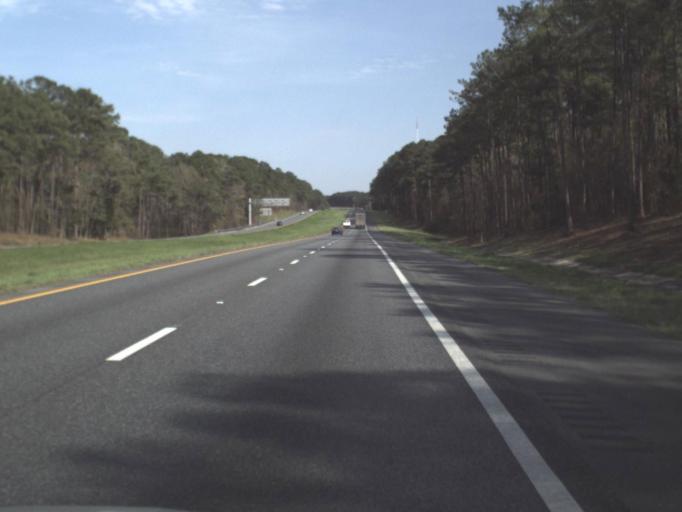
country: US
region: Florida
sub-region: Leon County
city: Tallahassee
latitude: 30.5000
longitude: -84.2224
